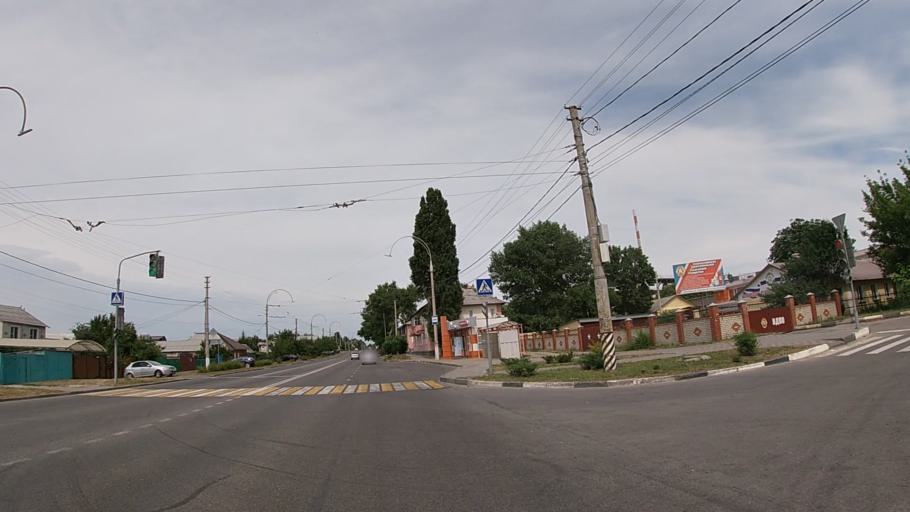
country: RU
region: Belgorod
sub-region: Belgorodskiy Rayon
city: Belgorod
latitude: 50.6058
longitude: 36.5540
